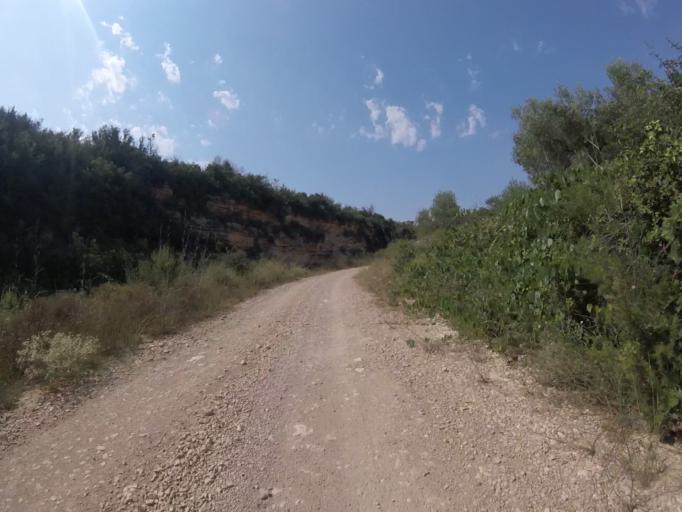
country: ES
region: Valencia
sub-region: Provincia de Castello
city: Alcala de Xivert
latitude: 40.3133
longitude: 0.1792
